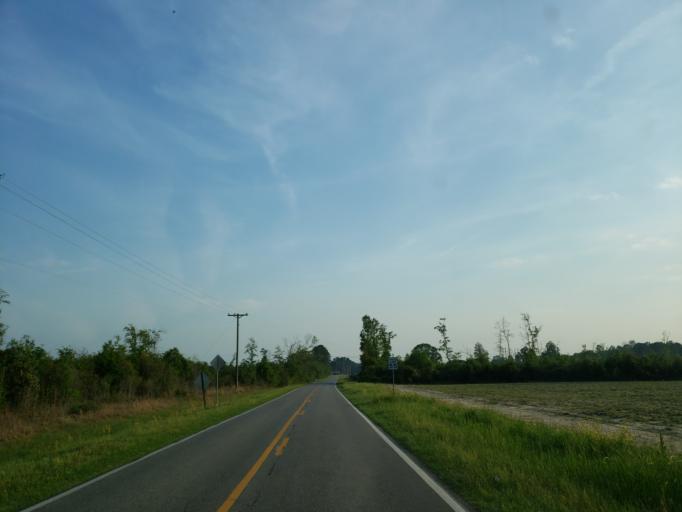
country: US
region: Georgia
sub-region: Cook County
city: Sparks
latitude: 31.2096
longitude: -83.4218
